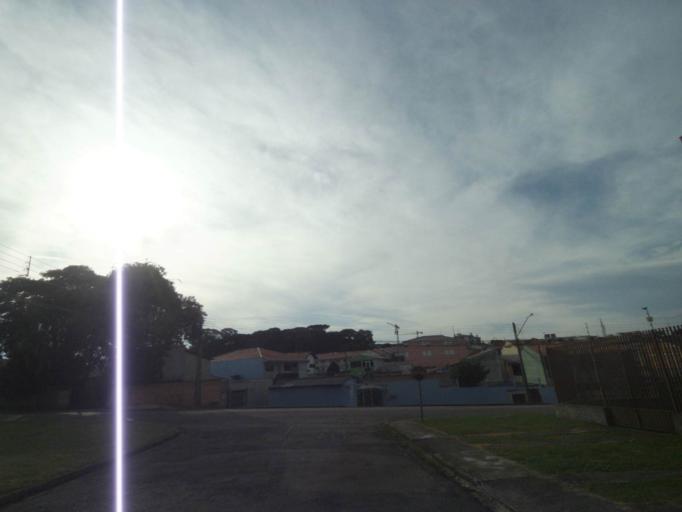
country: BR
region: Parana
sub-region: Pinhais
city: Pinhais
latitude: -25.4506
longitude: -49.2243
